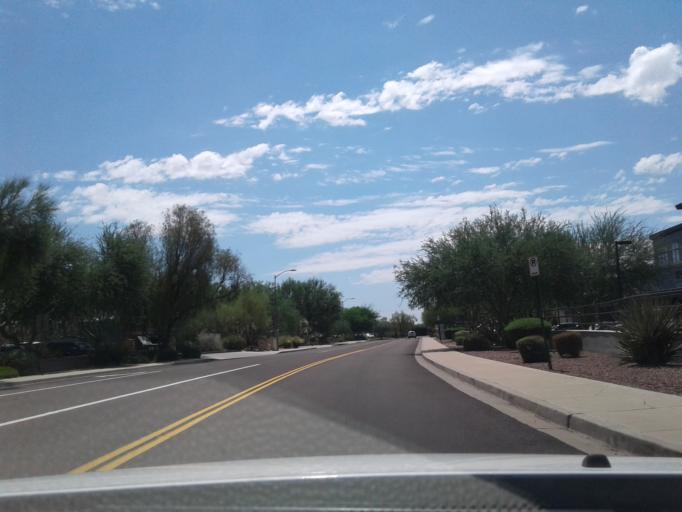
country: US
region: Arizona
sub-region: Maricopa County
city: Paradise Valley
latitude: 33.6275
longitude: -111.9169
